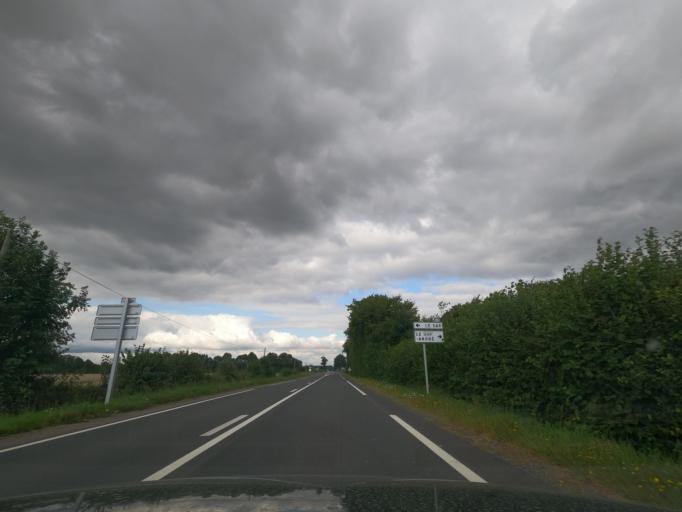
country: FR
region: Lower Normandy
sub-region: Departement de l'Orne
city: Gace
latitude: 48.8550
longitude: 0.3612
